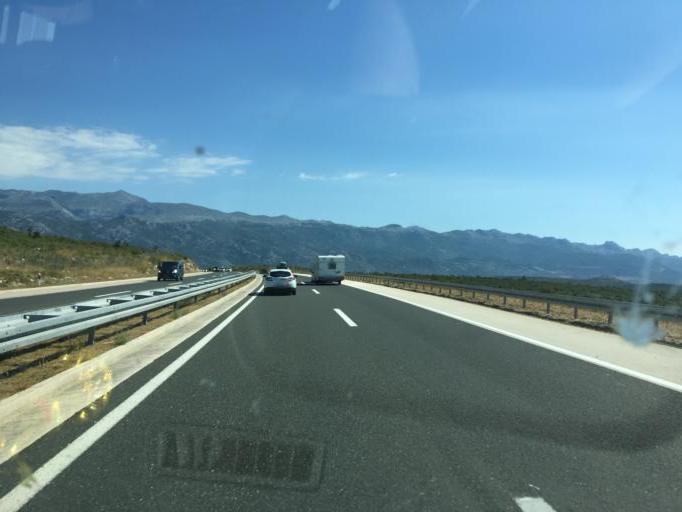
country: HR
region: Zadarska
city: Posedarje
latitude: 44.2243
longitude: 15.5069
